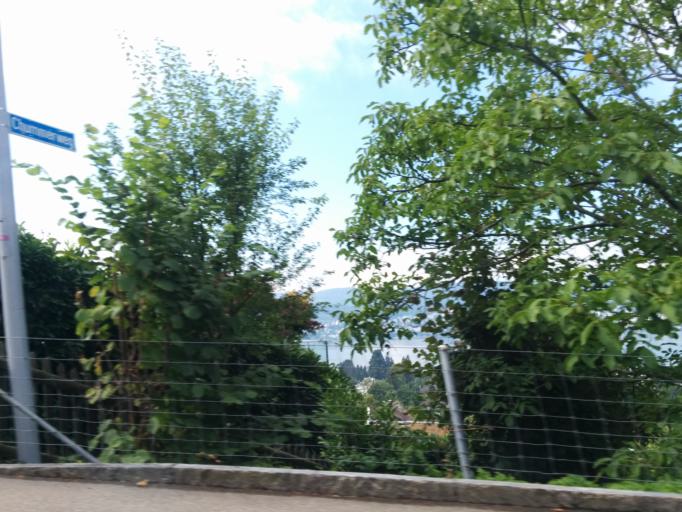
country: CH
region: Zurich
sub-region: Bezirk Meilen
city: Kuesnacht / Heslibach
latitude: 47.3125
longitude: 8.5917
